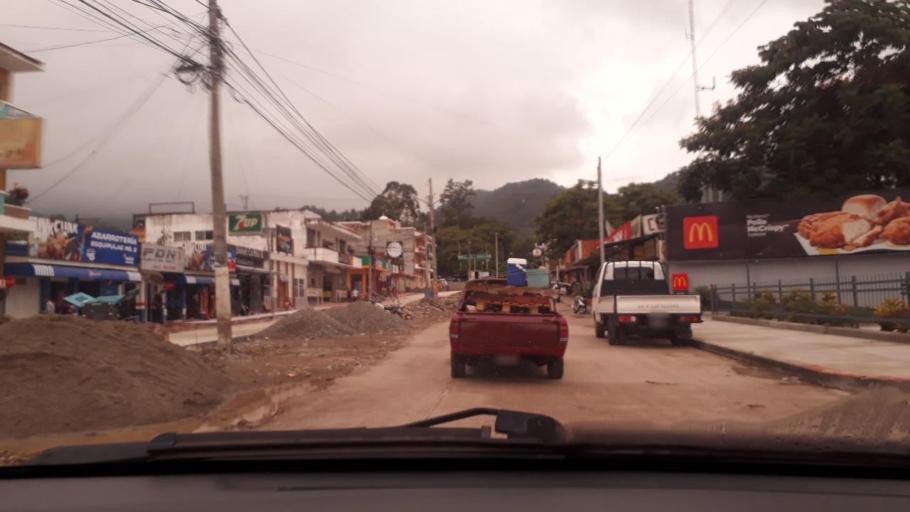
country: GT
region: Chiquimula
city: Esquipulas
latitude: 14.5627
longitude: -89.3529
